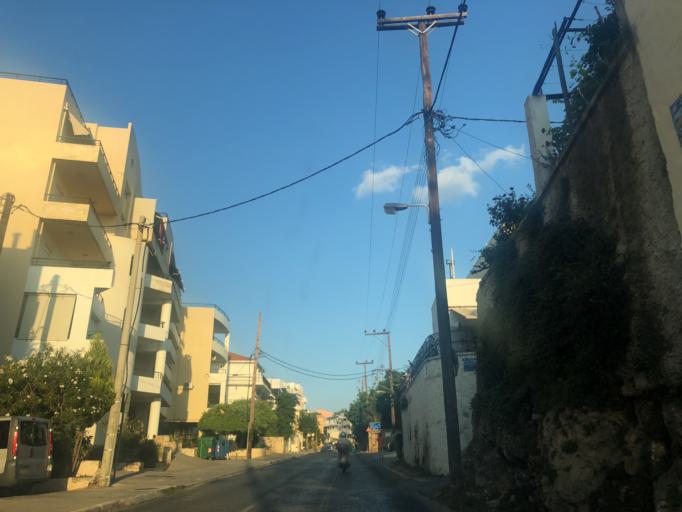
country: GR
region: Crete
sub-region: Nomos Chanias
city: Chania
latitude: 35.5157
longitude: 24.0365
